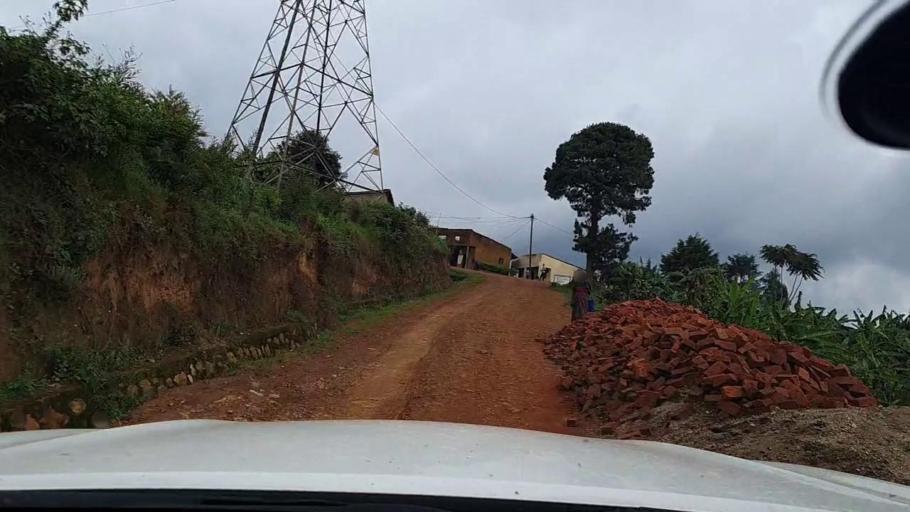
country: RW
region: Western Province
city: Kibuye
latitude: -2.1763
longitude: 29.4442
